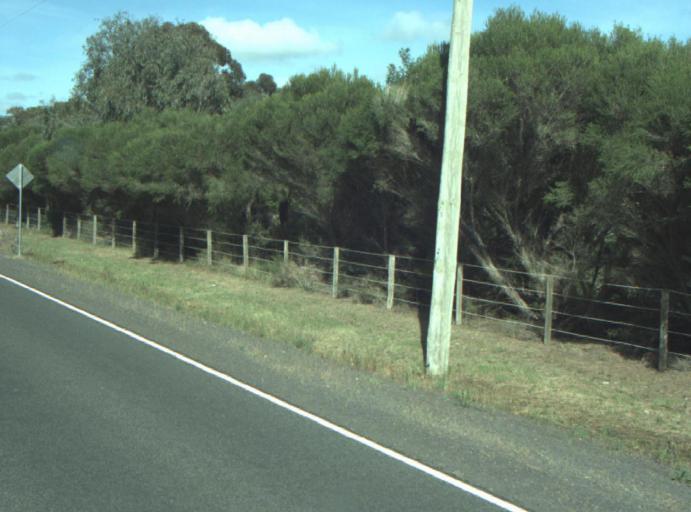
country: AU
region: Victoria
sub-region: Greater Geelong
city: Lara
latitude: -38.0102
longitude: 144.4285
